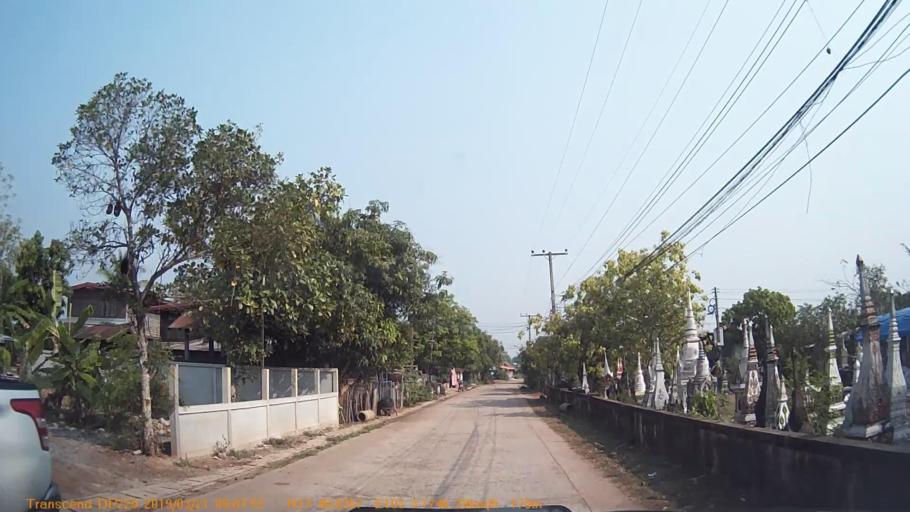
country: TH
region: Changwat Udon Thani
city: Phibun Rak
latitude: 17.6808
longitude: 103.0529
